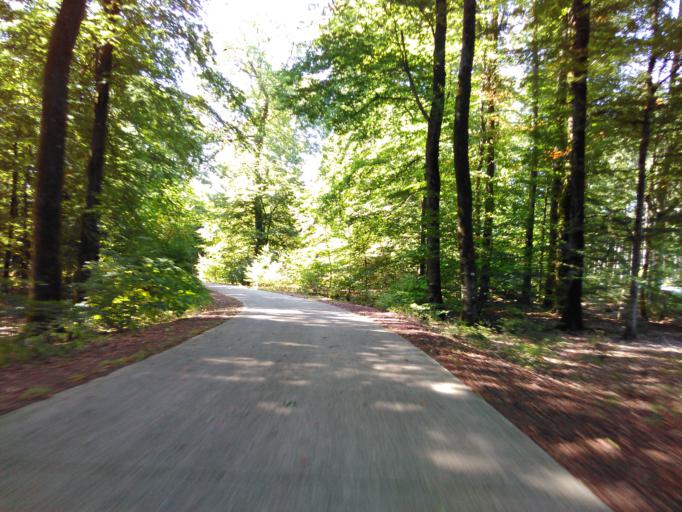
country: LU
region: Diekirch
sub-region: Canton de Redange
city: Rambrouch
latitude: 49.8411
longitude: 5.8097
